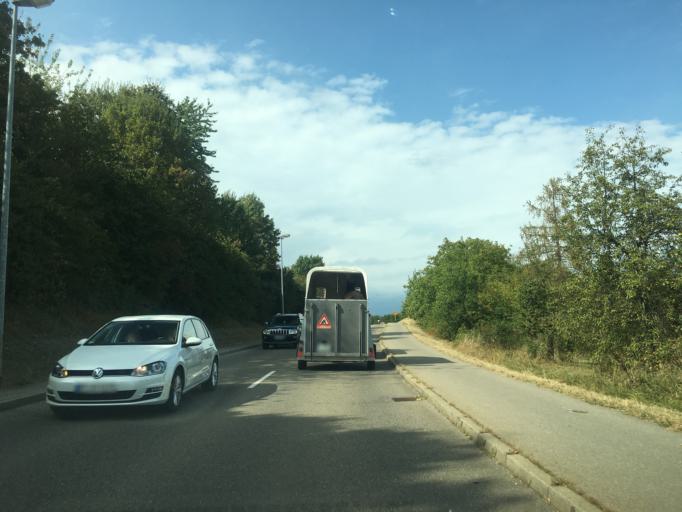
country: DE
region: Baden-Wuerttemberg
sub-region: Tuebingen Region
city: Wannweil
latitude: 48.4750
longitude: 9.1497
